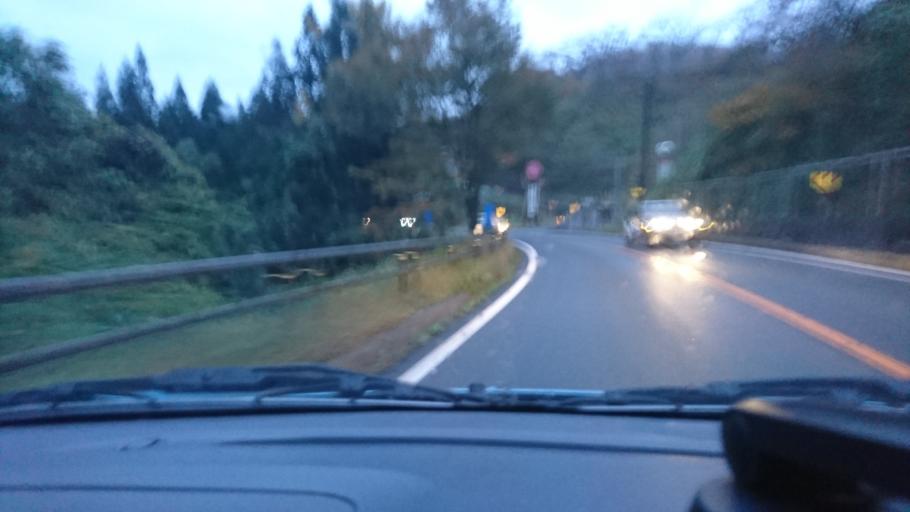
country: JP
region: Miyagi
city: Furukawa
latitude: 38.7382
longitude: 140.6981
